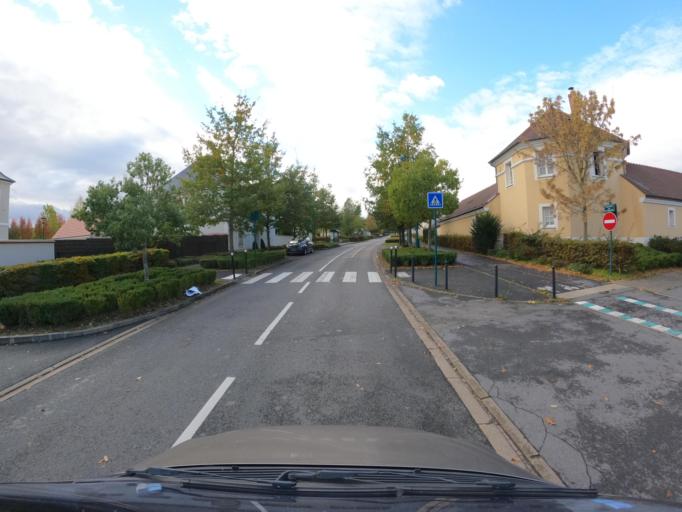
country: FR
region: Ile-de-France
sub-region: Departement de Seine-et-Marne
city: Magny-le-Hongre
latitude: 48.8730
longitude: 2.8146
